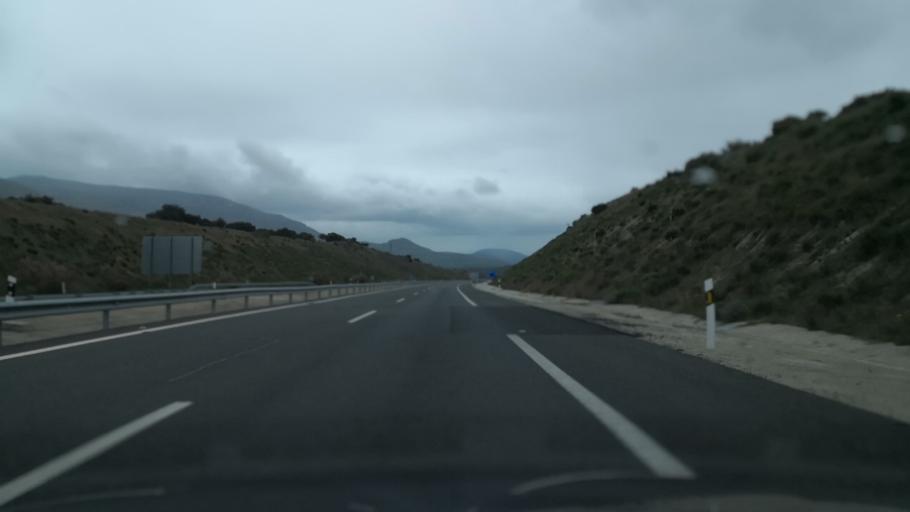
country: ES
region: Extremadura
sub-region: Provincia de Caceres
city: Jarilla
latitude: 40.2030
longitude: -5.9964
